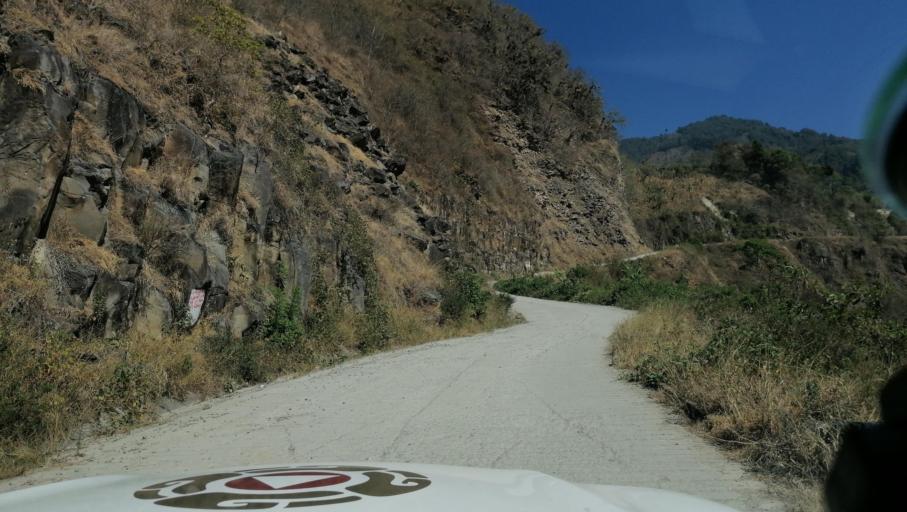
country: GT
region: San Marcos
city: Tacana
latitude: 15.1900
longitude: -92.1860
